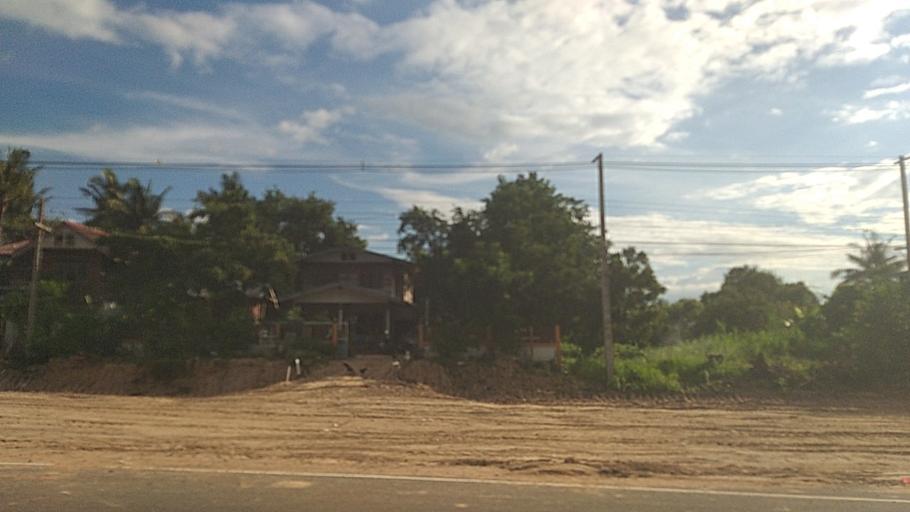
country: TH
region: Surin
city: Kap Choeng
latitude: 14.4819
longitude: 103.5834
